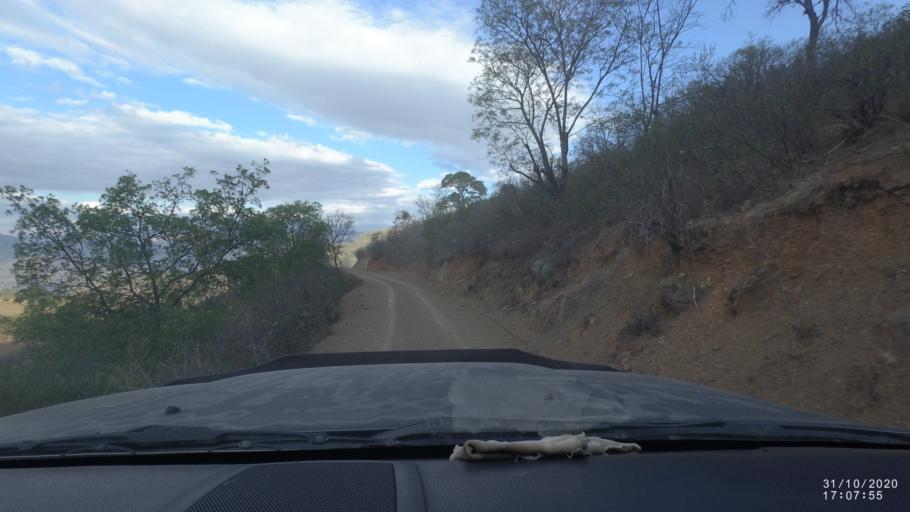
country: BO
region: Chuquisaca
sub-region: Provincia Zudanez
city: Mojocoya
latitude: -18.5457
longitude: -64.5419
